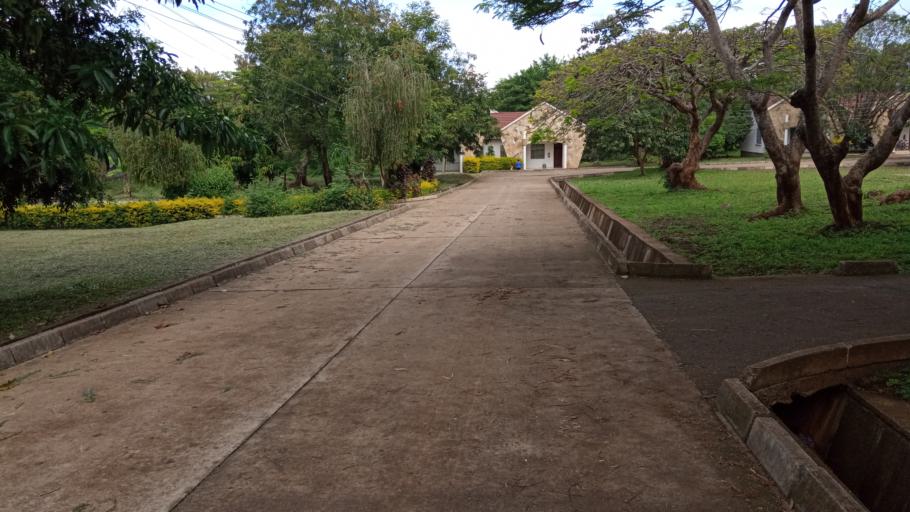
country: TZ
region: Arusha
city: Usa River
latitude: -3.3985
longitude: 36.8007
